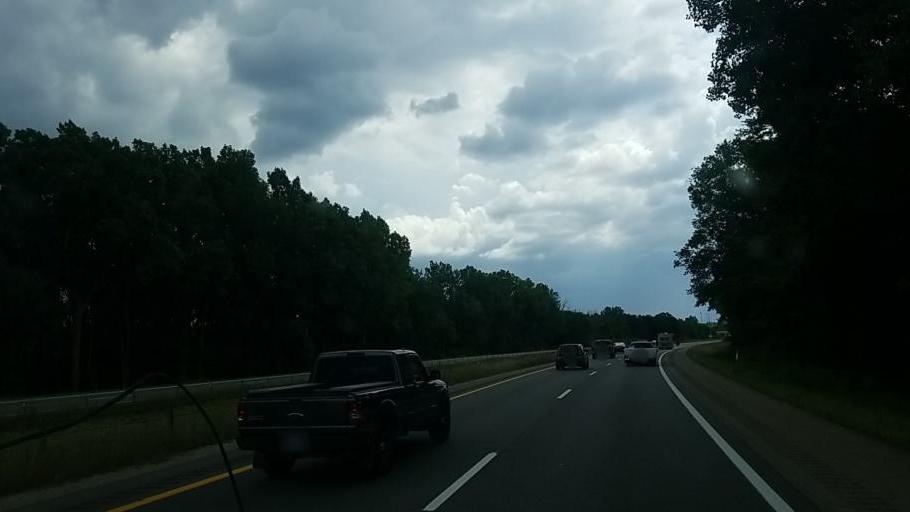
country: US
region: Michigan
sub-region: Kent County
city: Northview
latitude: 43.0065
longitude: -85.6053
